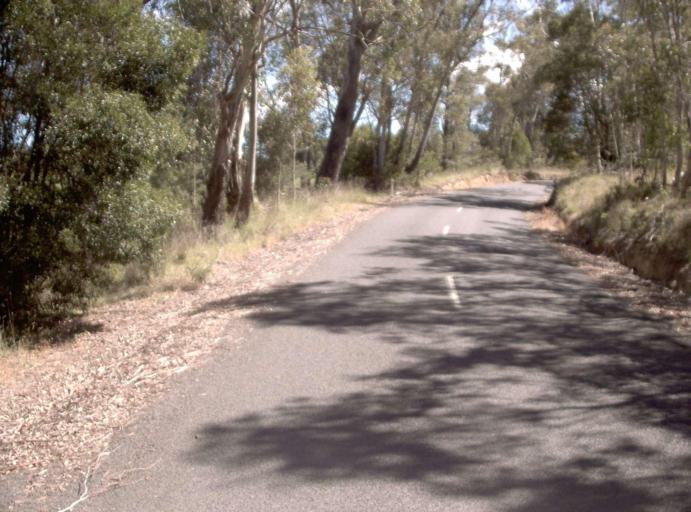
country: AU
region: New South Wales
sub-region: Bombala
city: Bombala
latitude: -37.0584
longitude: 148.8025
